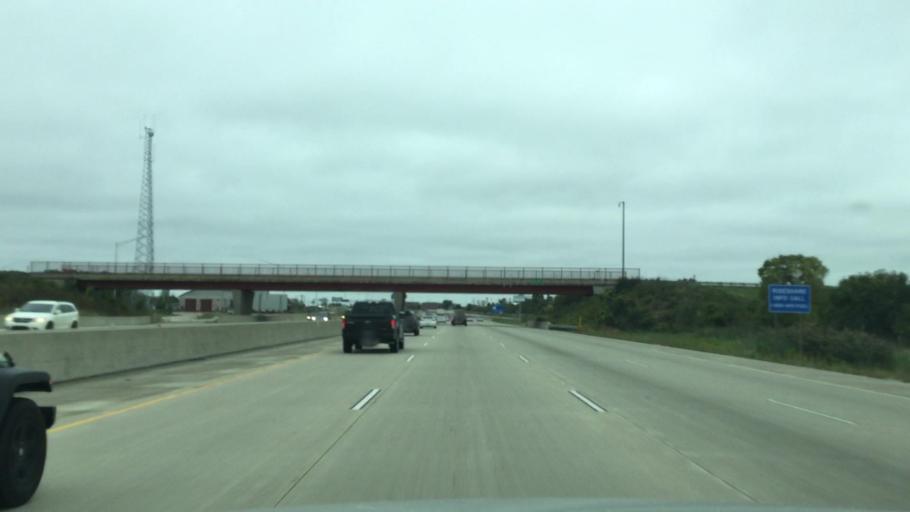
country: US
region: Wisconsin
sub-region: Kenosha County
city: Pleasant Prairie
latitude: 42.5034
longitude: -87.9516
